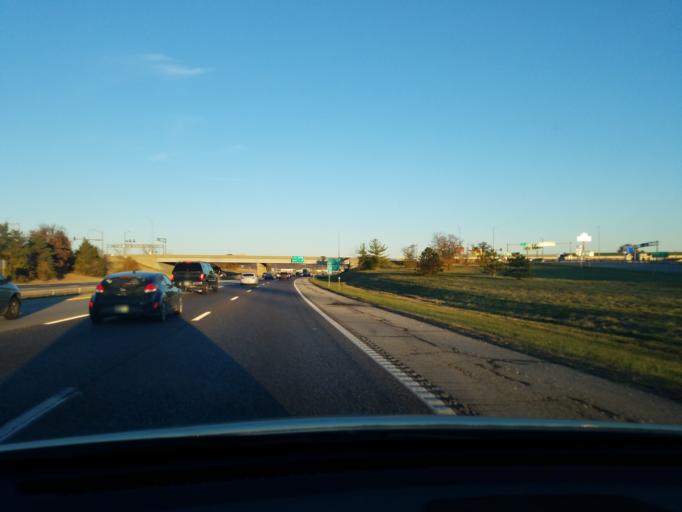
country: US
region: Missouri
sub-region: Saint Louis County
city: Valley Park
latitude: 38.5422
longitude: -90.4718
